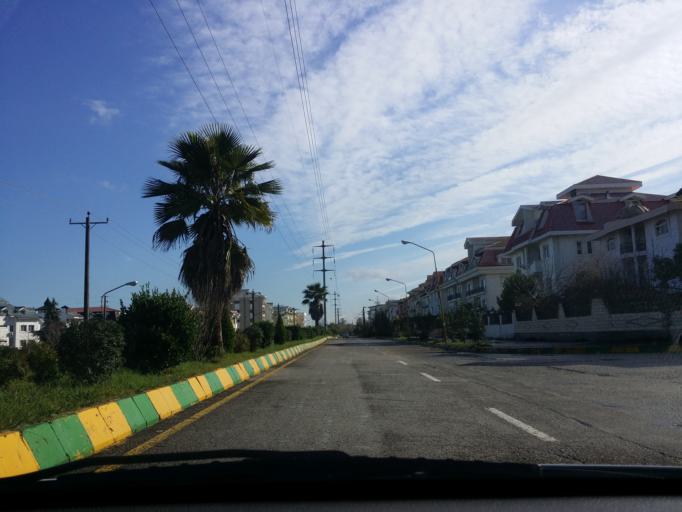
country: IR
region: Mazandaran
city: Chalus
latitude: 36.6751
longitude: 51.3091
